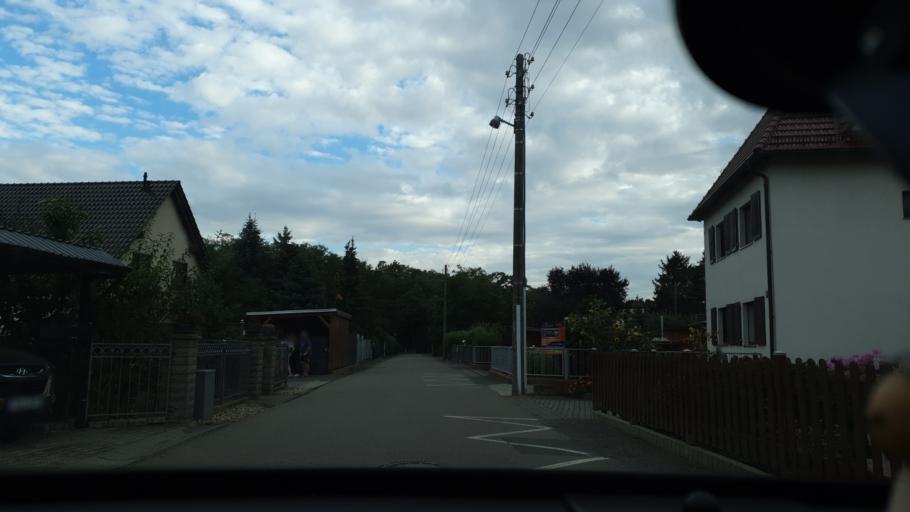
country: DE
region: Saxony
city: Torgau
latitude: 51.5468
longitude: 12.9930
